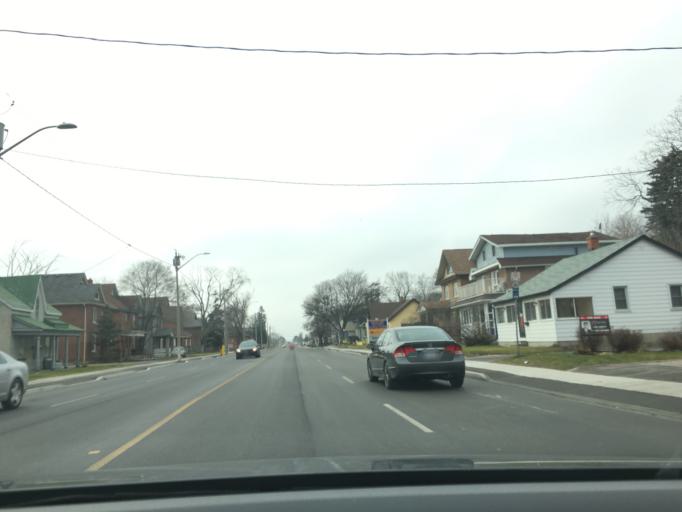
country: CA
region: Ontario
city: Barrie
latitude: 44.3857
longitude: -79.6986
